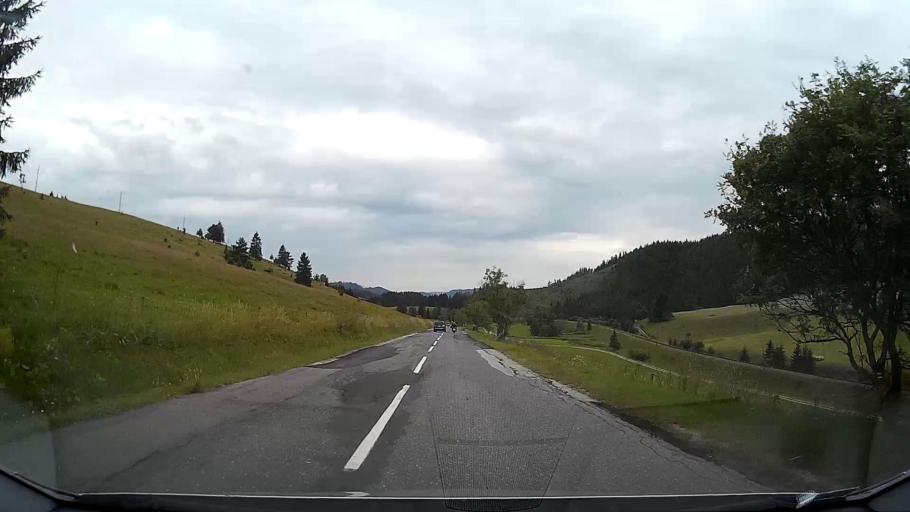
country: SK
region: Kosicky
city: Dobsina
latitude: 48.8603
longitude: 20.2196
